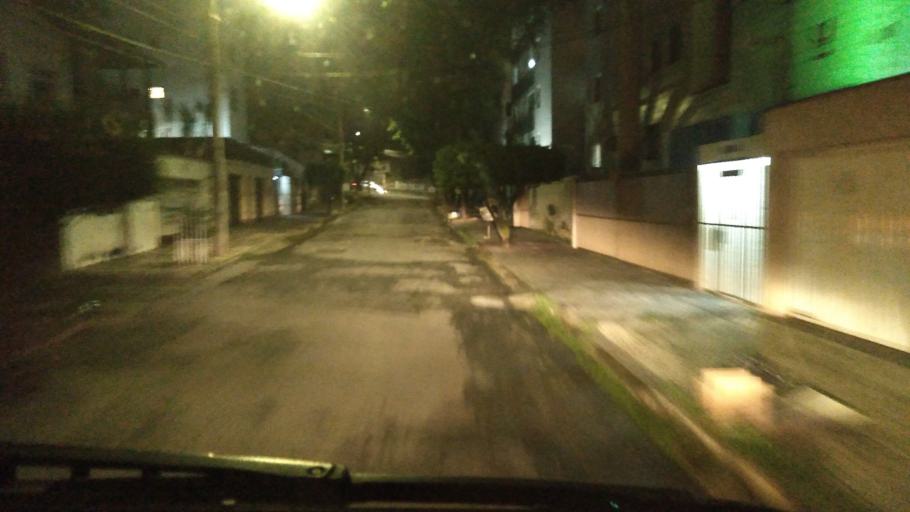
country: BR
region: Minas Gerais
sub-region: Belo Horizonte
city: Belo Horizonte
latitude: -19.8718
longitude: -43.9314
